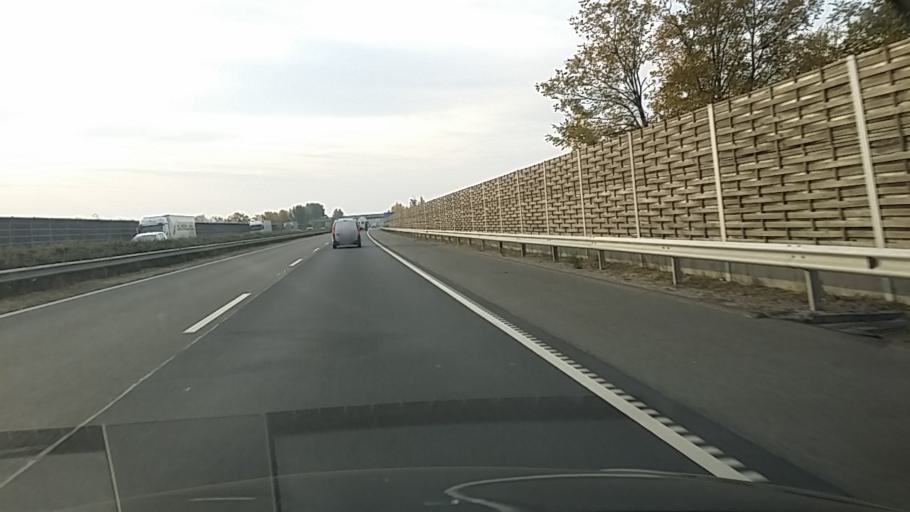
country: HU
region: Bacs-Kiskun
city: Lajosmizse
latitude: 47.0061
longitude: 19.6028
